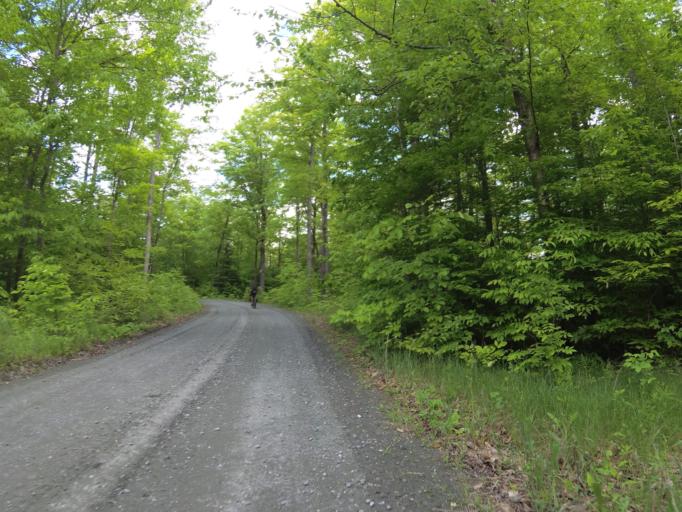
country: CA
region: Ontario
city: Renfrew
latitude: 45.0670
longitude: -76.8021
